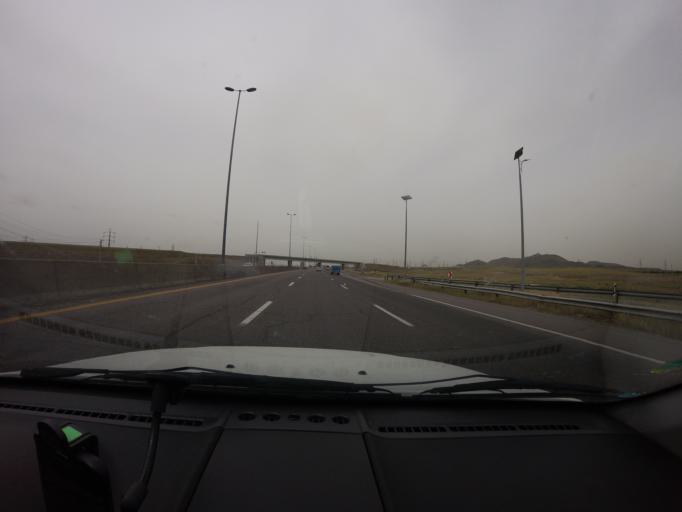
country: IR
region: Tehran
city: Robat Karim
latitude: 35.4700
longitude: 51.0243
